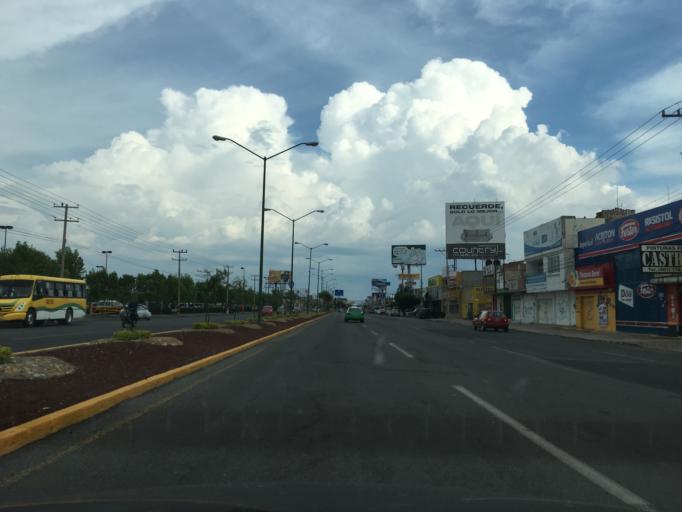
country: MX
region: Guanajuato
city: Celaya
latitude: 20.5461
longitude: -100.8215
